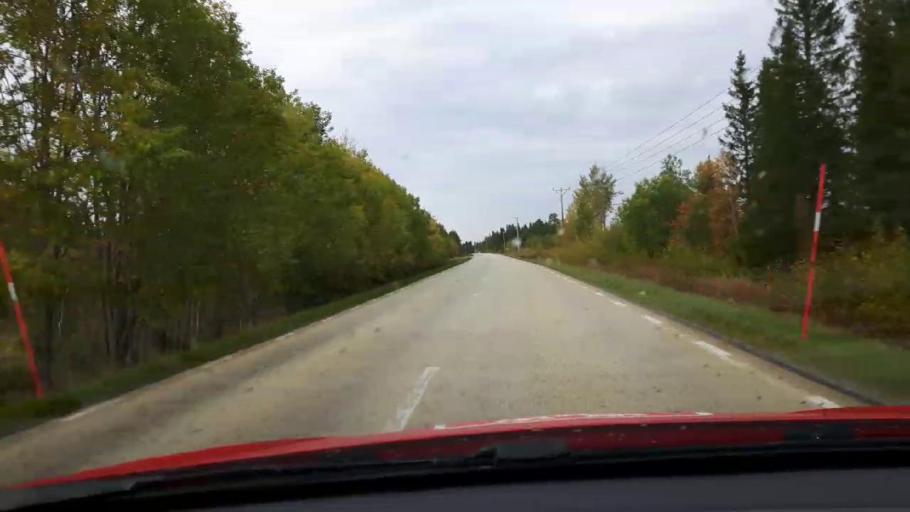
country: SE
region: Jaemtland
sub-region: Bergs Kommun
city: Hoverberg
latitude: 62.9623
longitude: 14.3474
